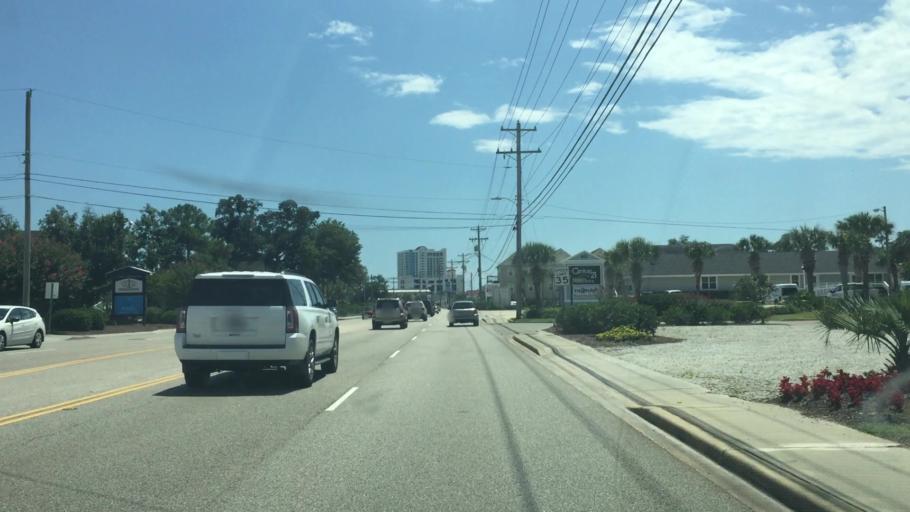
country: US
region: South Carolina
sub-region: Horry County
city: North Myrtle Beach
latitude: 33.8358
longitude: -78.6447
